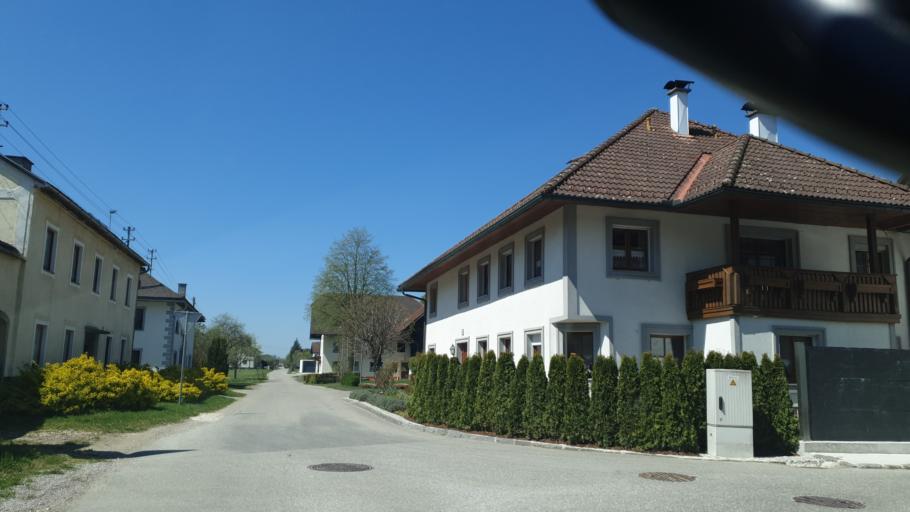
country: AT
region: Upper Austria
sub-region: Politischer Bezirk Vocklabruck
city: Gampern
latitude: 47.9964
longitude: 13.5589
